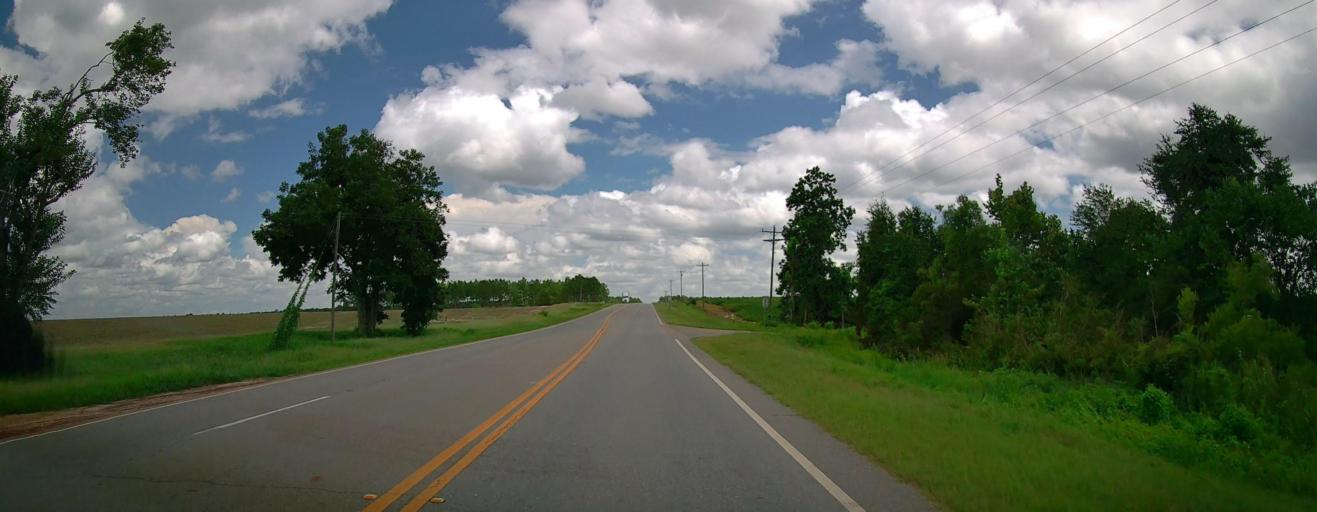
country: US
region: Georgia
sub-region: Turner County
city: Ashburn
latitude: 31.7220
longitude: -83.5400
